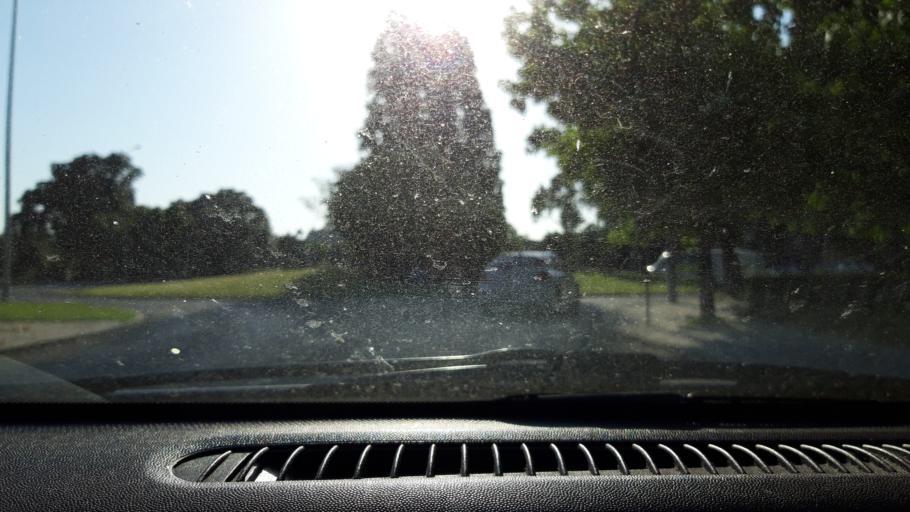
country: PT
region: Santarem
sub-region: Torres Novas
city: Torres Novas
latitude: 39.4745
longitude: -8.5477
